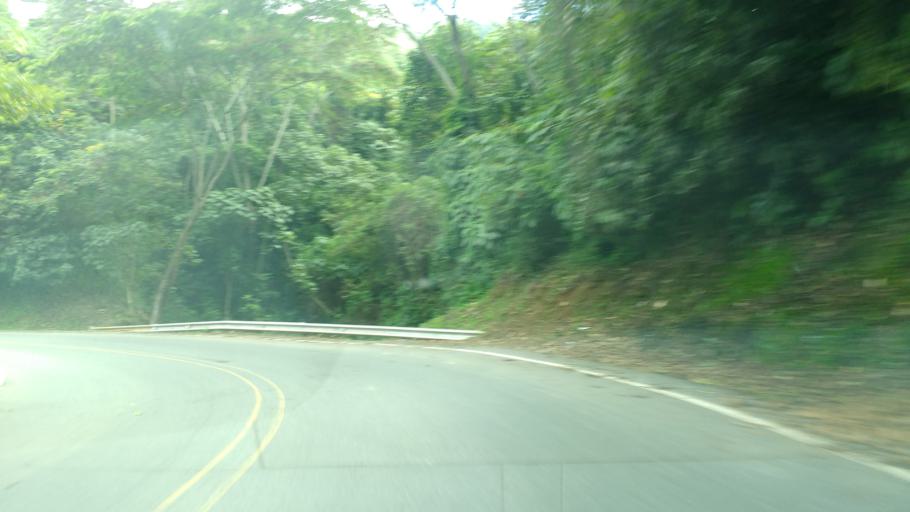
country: CO
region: Antioquia
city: Amaga
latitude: 6.0606
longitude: -75.7446
